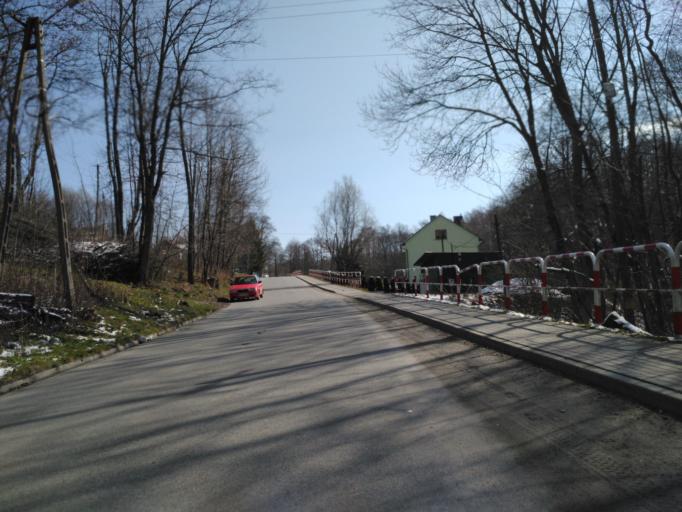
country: PL
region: Subcarpathian Voivodeship
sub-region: Powiat ropczycko-sedziszowski
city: Wielopole Skrzynskie
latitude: 49.9862
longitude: 21.5912
